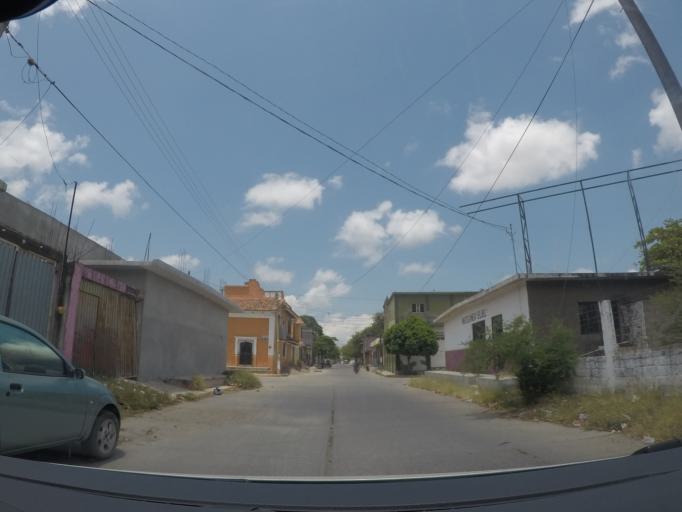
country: MX
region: Oaxaca
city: Juchitan de Zaragoza
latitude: 16.4409
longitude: -95.0183
